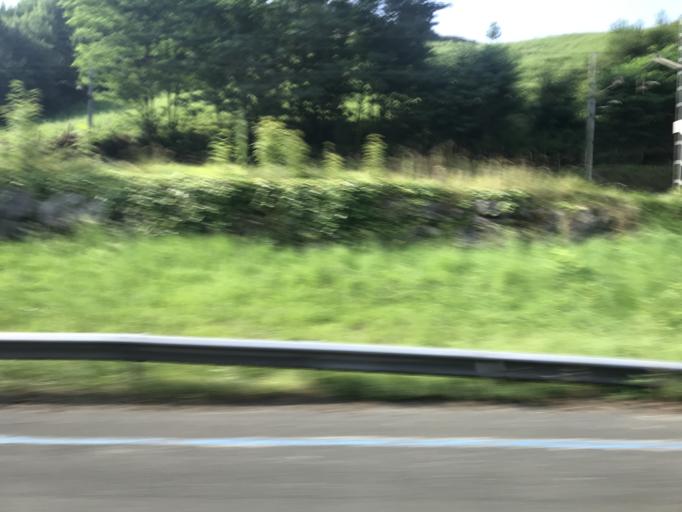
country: ES
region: Basque Country
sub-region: Provincia de Guipuzcoa
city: Aduna
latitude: 43.1962
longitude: -2.0444
